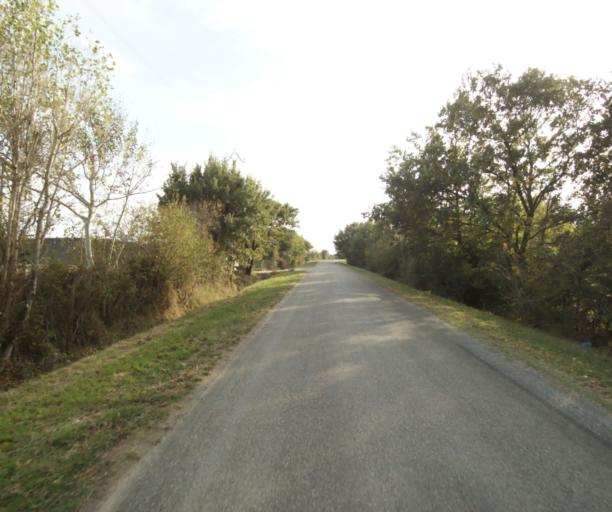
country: FR
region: Midi-Pyrenees
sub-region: Departement du Tarn-et-Garonne
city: Campsas
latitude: 43.8755
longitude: 1.3202
